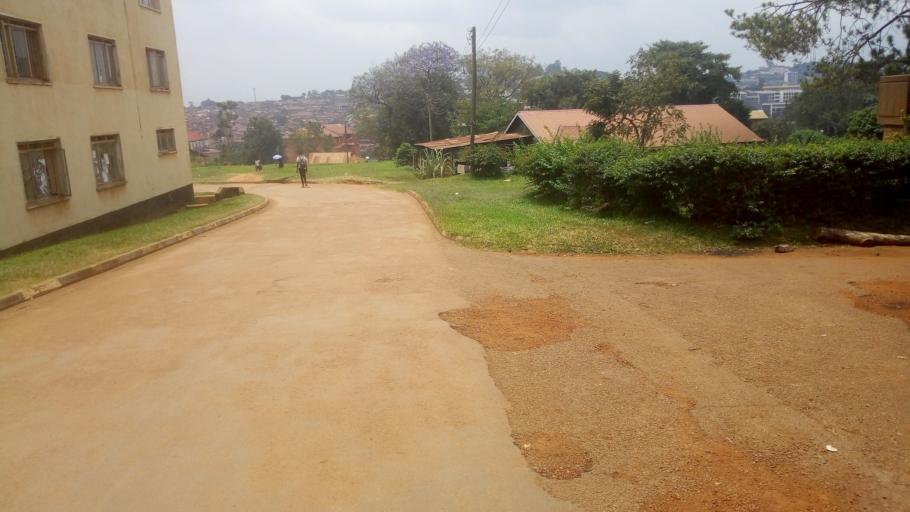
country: UG
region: Central Region
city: Kampala Central Division
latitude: 0.3384
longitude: 32.5685
